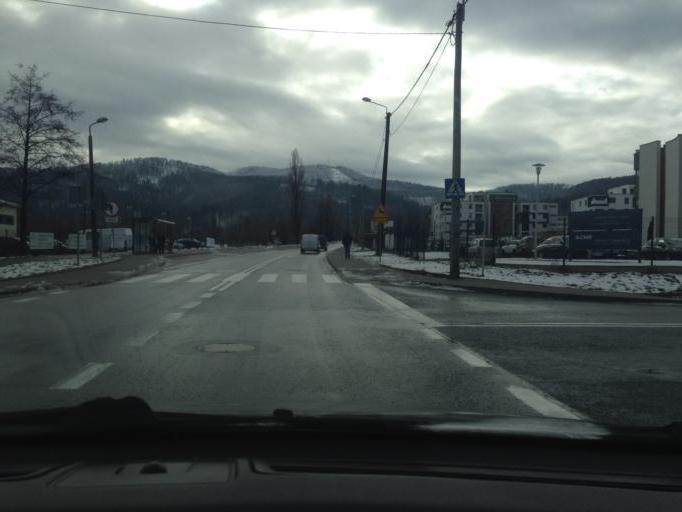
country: PL
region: Silesian Voivodeship
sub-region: Powiat bielski
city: Bystra
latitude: 49.7859
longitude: 19.0313
